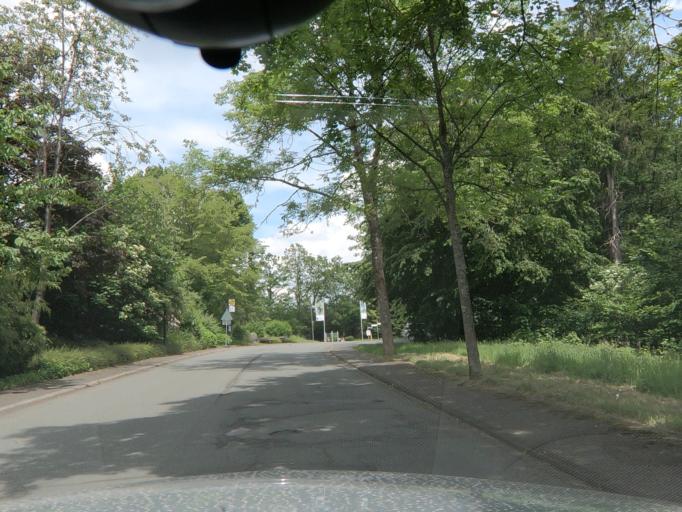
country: DE
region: North Rhine-Westphalia
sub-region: Regierungsbezirk Arnsberg
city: Bestwig
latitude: 51.3745
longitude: 8.3400
